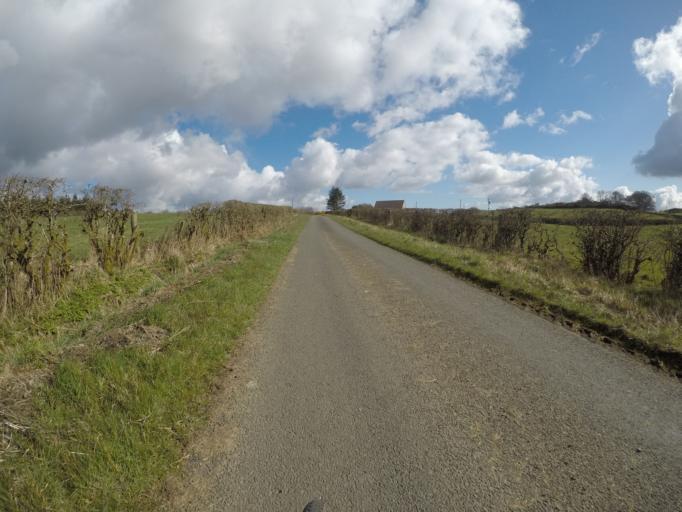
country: GB
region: Scotland
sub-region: North Ayrshire
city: Beith
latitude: 55.7063
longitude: -4.6629
